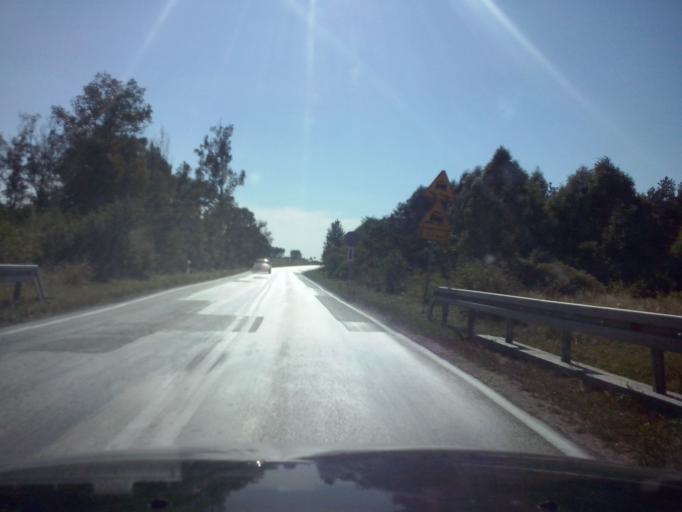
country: PL
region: Swietokrzyskie
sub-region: Powiat pinczowski
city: Kije
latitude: 50.6009
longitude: 20.6541
